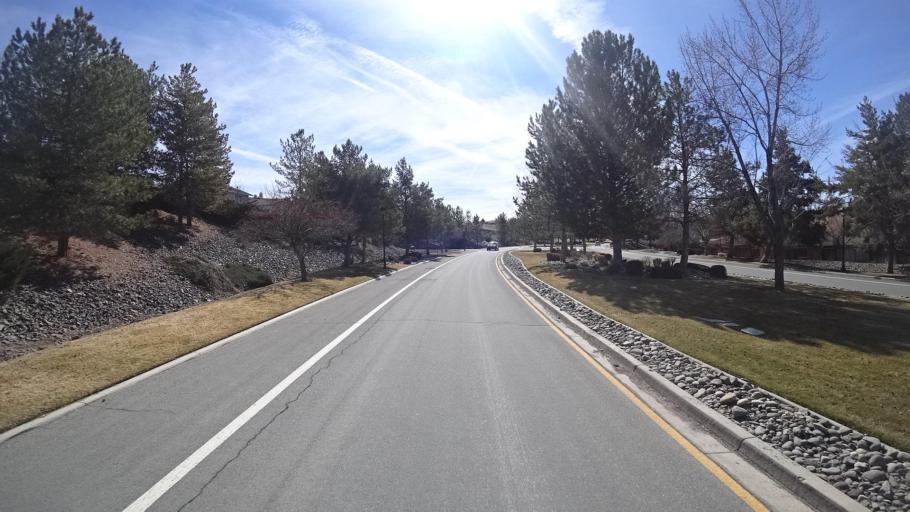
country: US
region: Nevada
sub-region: Washoe County
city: Spanish Springs
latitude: 39.5838
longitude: -119.7042
